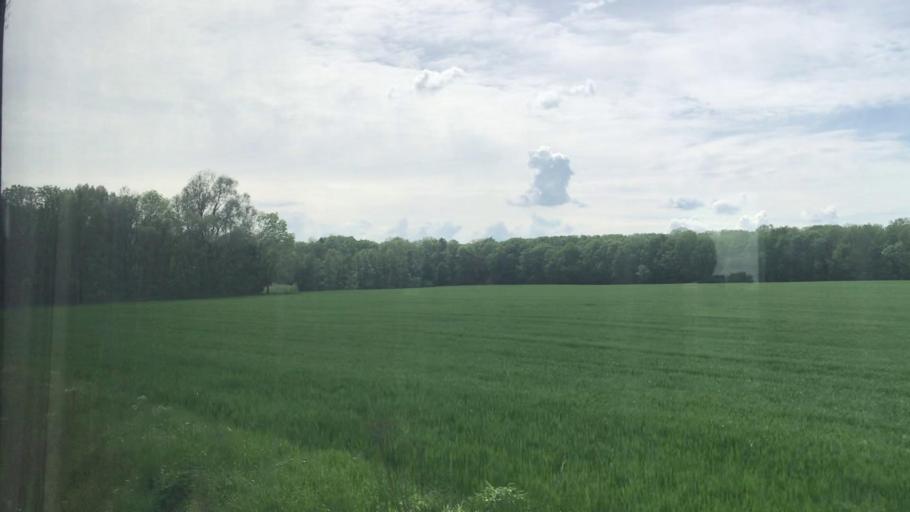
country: PL
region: Lower Silesian Voivodeship
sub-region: Powiat wroclawski
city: Katy Wroclawskie
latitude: 51.0136
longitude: 16.6995
